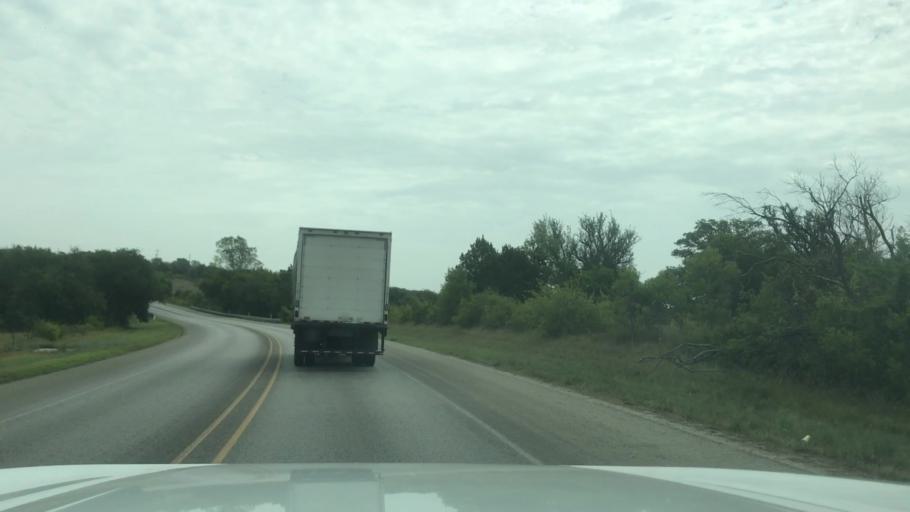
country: US
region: Texas
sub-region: Erath County
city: Dublin
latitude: 32.0876
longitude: -98.4335
